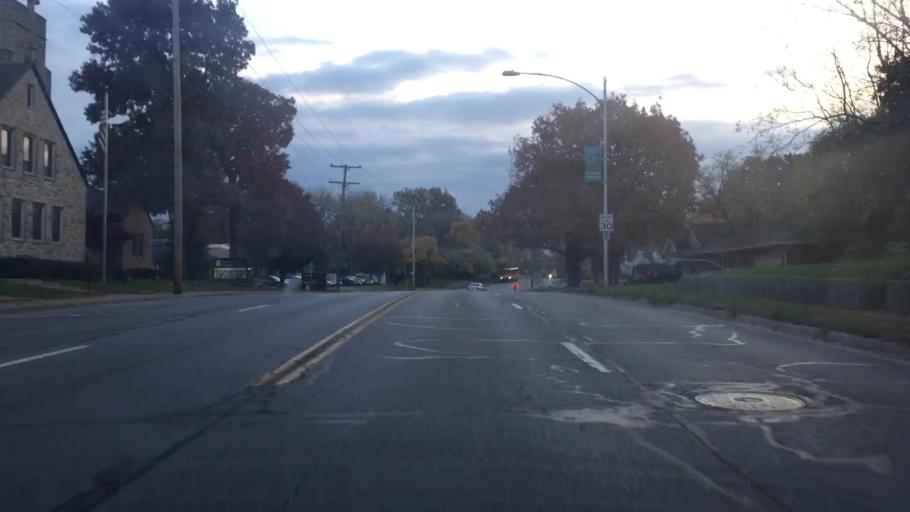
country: US
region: Kansas
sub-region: Johnson County
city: Merriam
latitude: 39.0229
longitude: -94.7110
